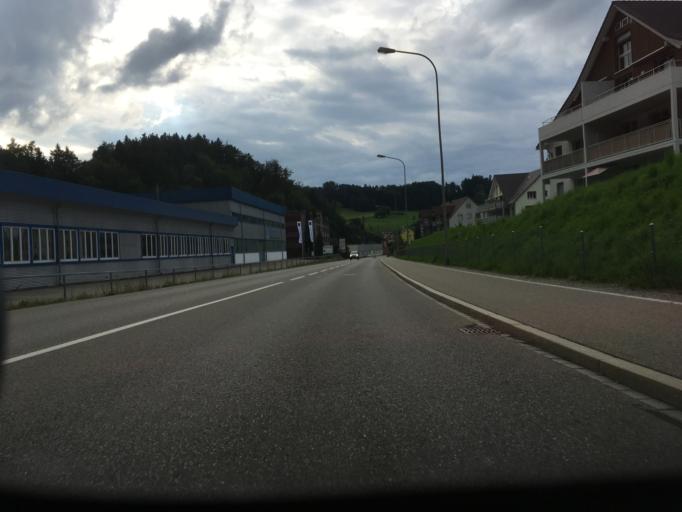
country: CH
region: Zurich
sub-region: Bezirk Pfaeffikon
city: Bauma
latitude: 47.3690
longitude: 8.8711
